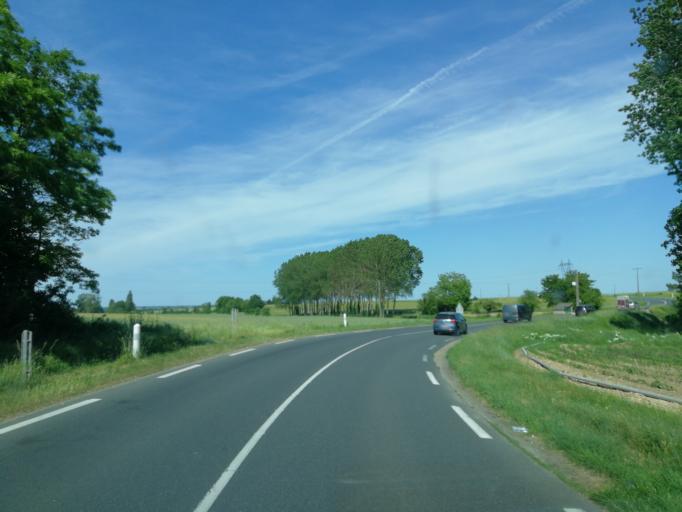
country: FR
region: Poitou-Charentes
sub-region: Departement de la Vienne
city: Loudun
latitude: 47.0659
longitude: 0.1629
